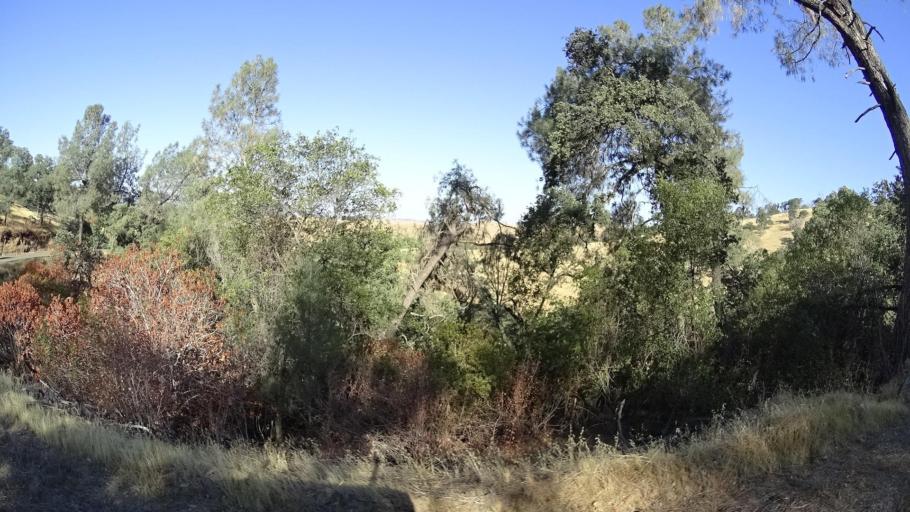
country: US
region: California
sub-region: Mariposa County
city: Mariposa
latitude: 37.5536
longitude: -120.1746
